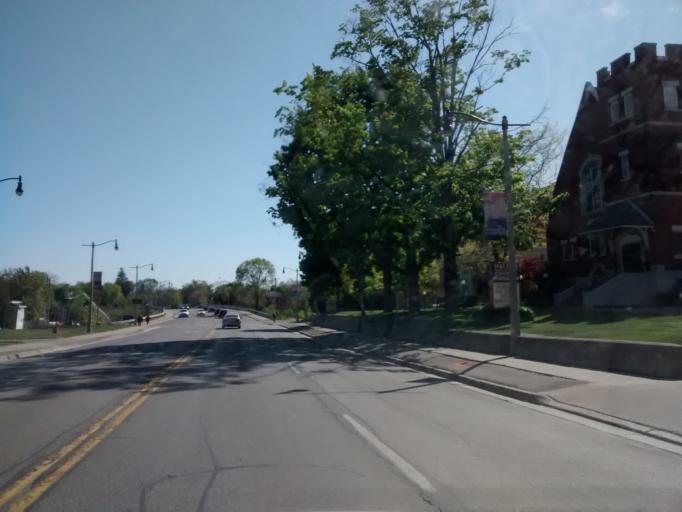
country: CA
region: Ontario
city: Oakville
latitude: 43.3937
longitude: -79.7126
